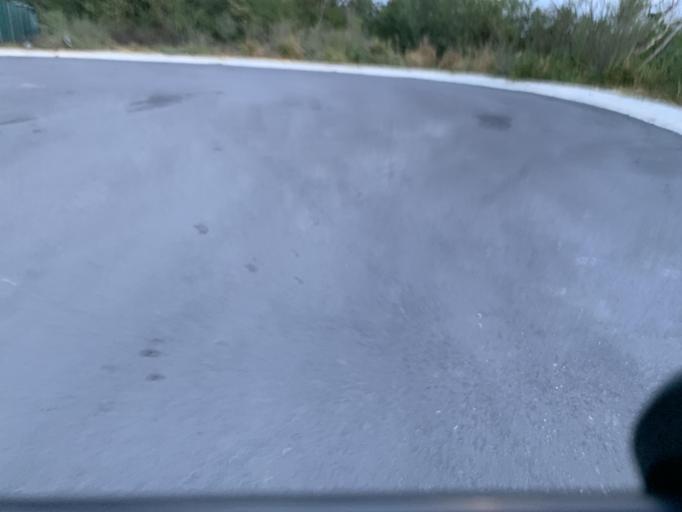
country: MX
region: Nuevo Leon
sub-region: Juarez
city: Bosques de San Pedro
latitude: 25.5243
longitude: -100.1903
